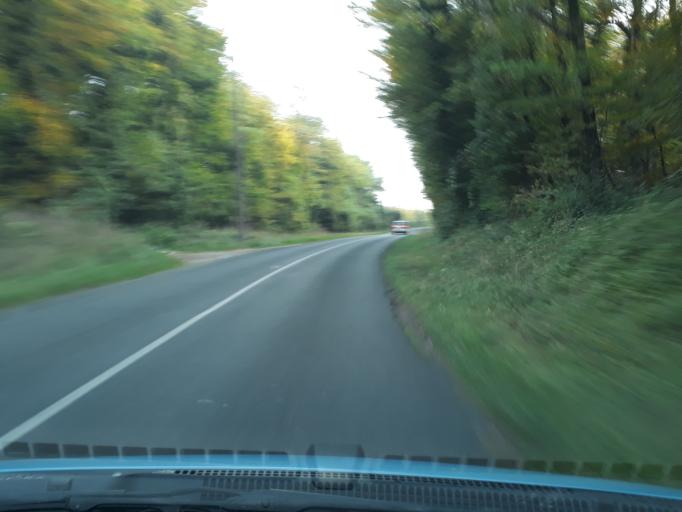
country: FR
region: Ile-de-France
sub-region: Departement de Seine-et-Marne
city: Moret-sur-Loing
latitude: 48.3608
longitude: 2.8038
